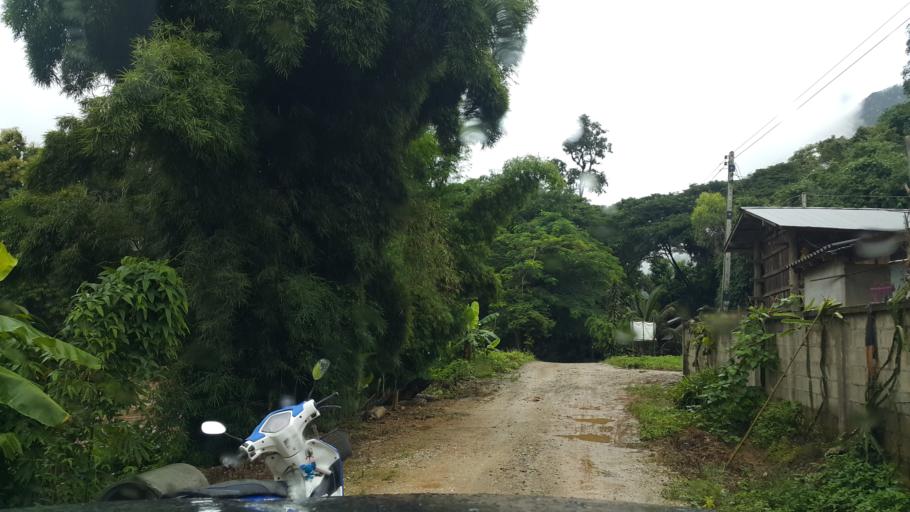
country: TH
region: Phayao
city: Chiang Kham
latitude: 19.4966
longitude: 100.4617
